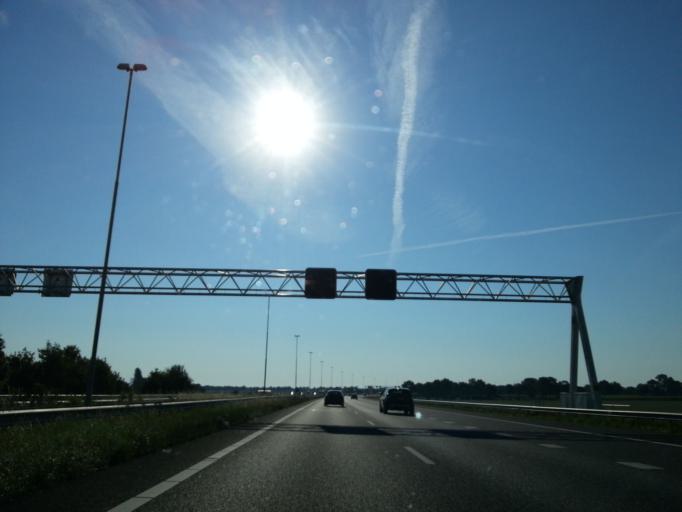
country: NL
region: North Brabant
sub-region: Gemeente Dongen
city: Dongen
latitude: 51.5504
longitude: 4.9618
